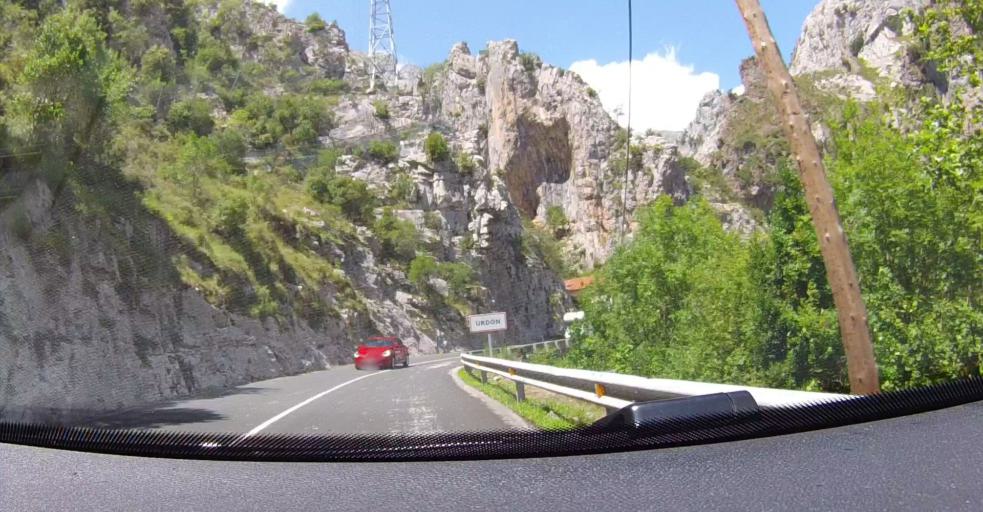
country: ES
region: Cantabria
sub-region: Provincia de Cantabria
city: Tresviso
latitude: 43.2664
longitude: -4.6312
